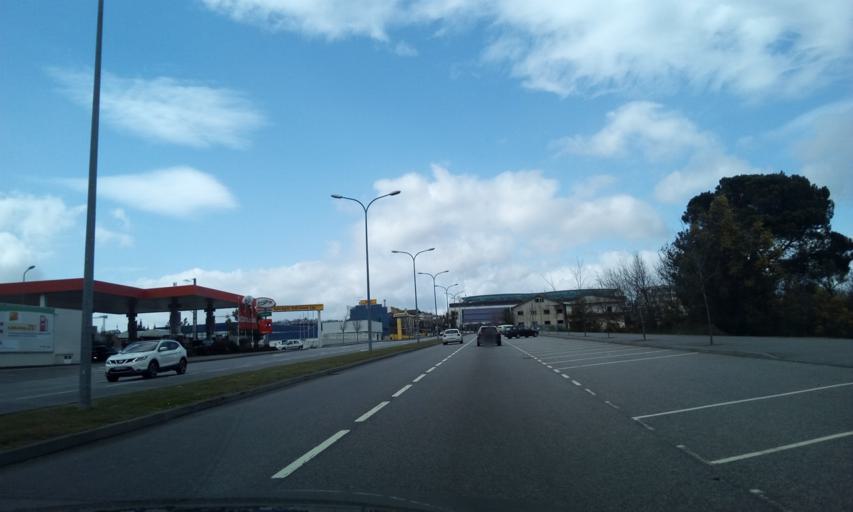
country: PT
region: Viseu
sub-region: Viseu
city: Viseu
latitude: 40.6373
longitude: -7.9092
